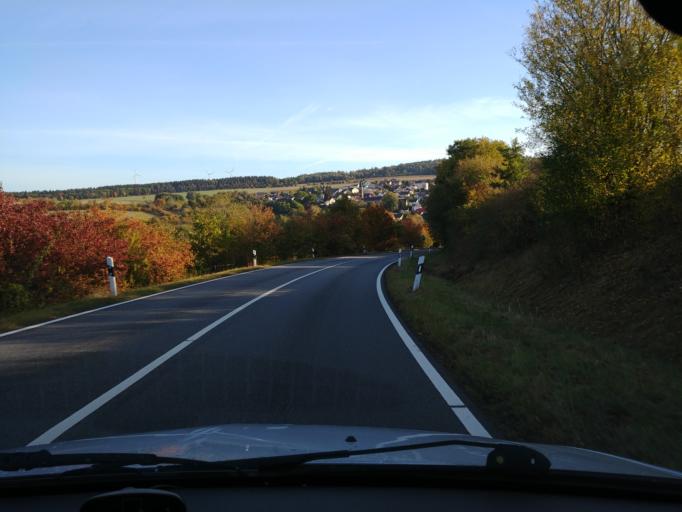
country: DE
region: Hesse
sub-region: Regierungsbezirk Darmstadt
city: Waldems
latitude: 50.2700
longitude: 8.3353
